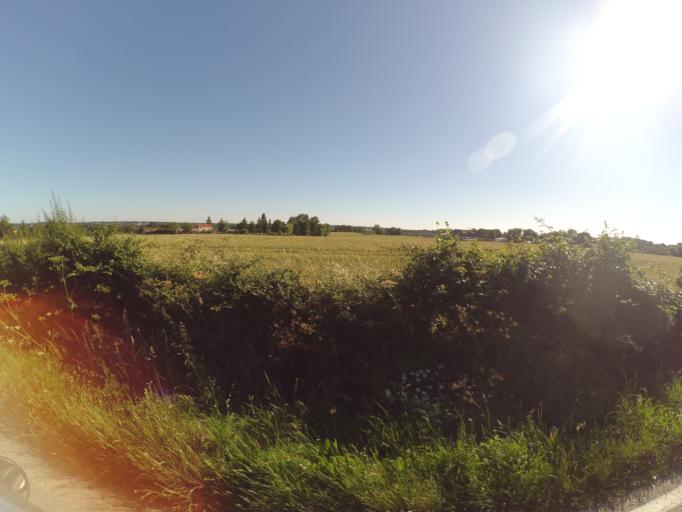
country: FR
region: Pays de la Loire
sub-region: Departement de la Vendee
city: Saint-Paul-en-Pareds
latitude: 46.8616
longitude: -0.9702
